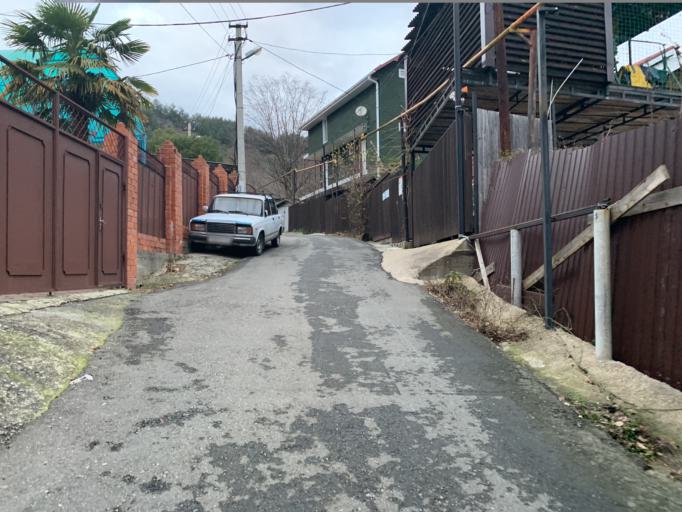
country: RU
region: Krasnodarskiy
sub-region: Sochi City
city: Lazarevskoye
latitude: 43.9228
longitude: 39.3236
